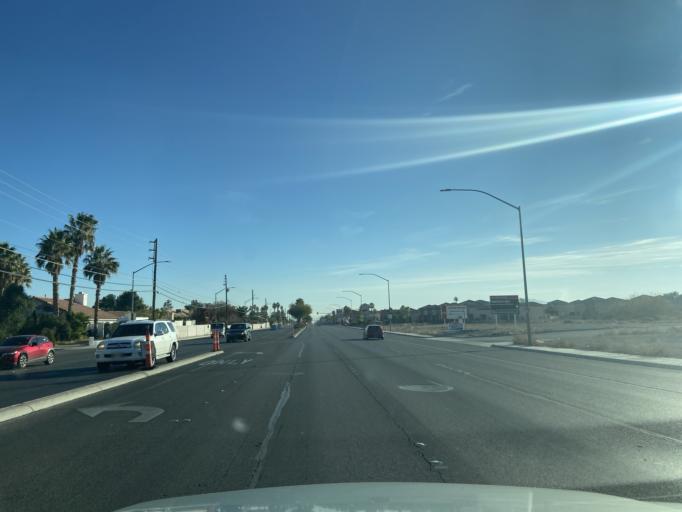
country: US
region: Nevada
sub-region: Clark County
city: North Las Vegas
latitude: 36.2393
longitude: -115.1882
